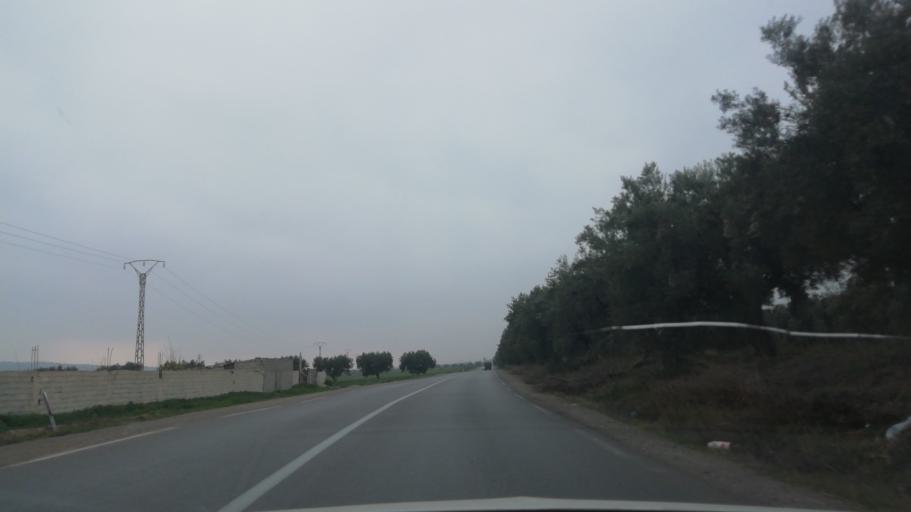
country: DZ
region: Sidi Bel Abbes
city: Sfizef
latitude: 35.2666
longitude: -0.1640
